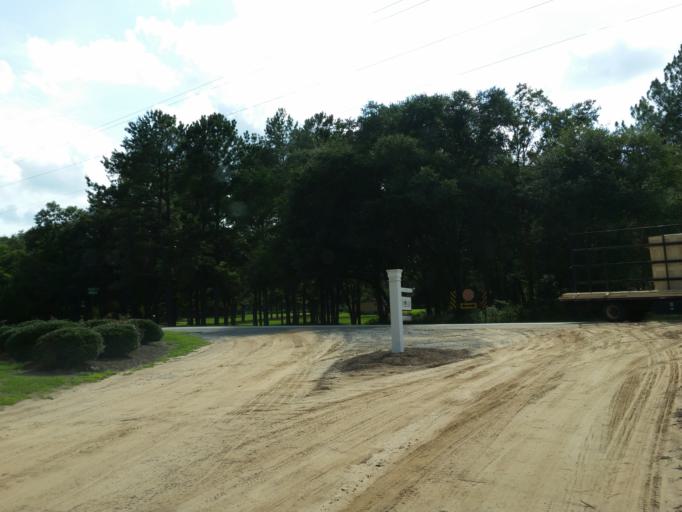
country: US
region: Georgia
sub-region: Lee County
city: Leesburg
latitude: 31.7482
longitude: -84.0397
